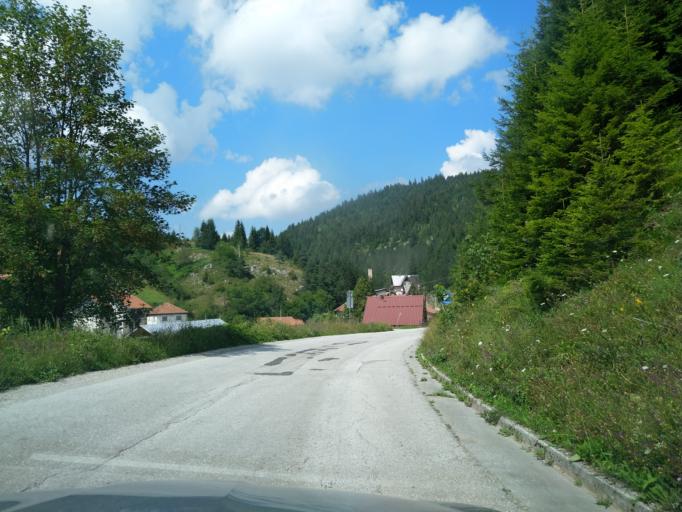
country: RS
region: Central Serbia
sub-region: Zlatiborski Okrug
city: Nova Varos
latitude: 43.5454
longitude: 19.9022
